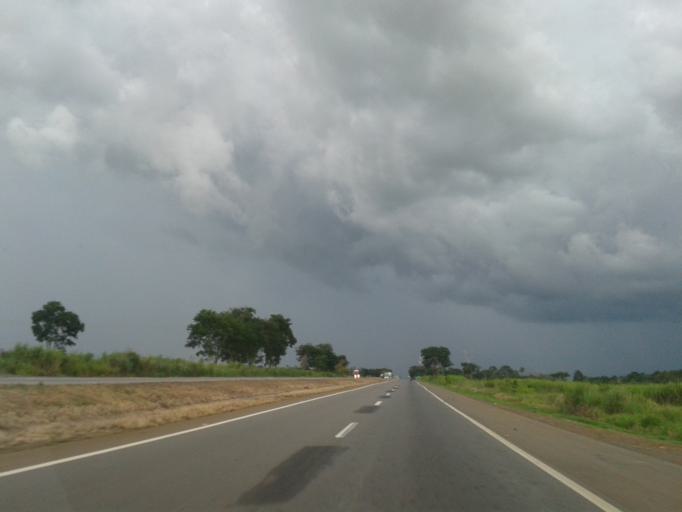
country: BR
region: Goias
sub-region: Morrinhos
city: Morrinhos
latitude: -17.5476
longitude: -49.2078
